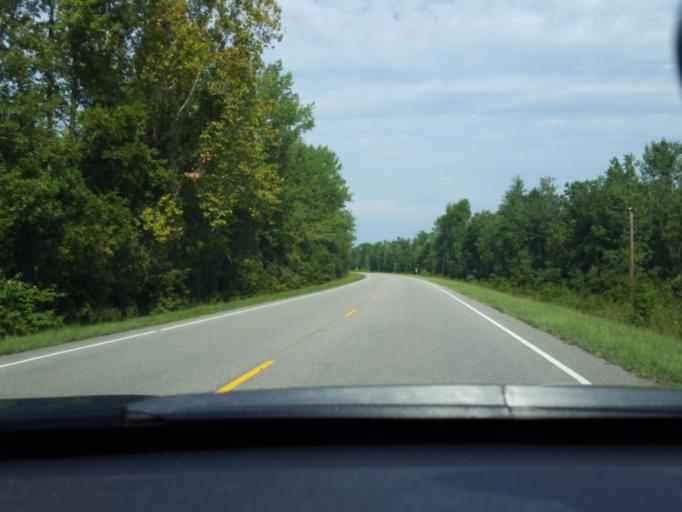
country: US
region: North Carolina
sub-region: Washington County
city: Plymouth
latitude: 35.9084
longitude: -76.7157
